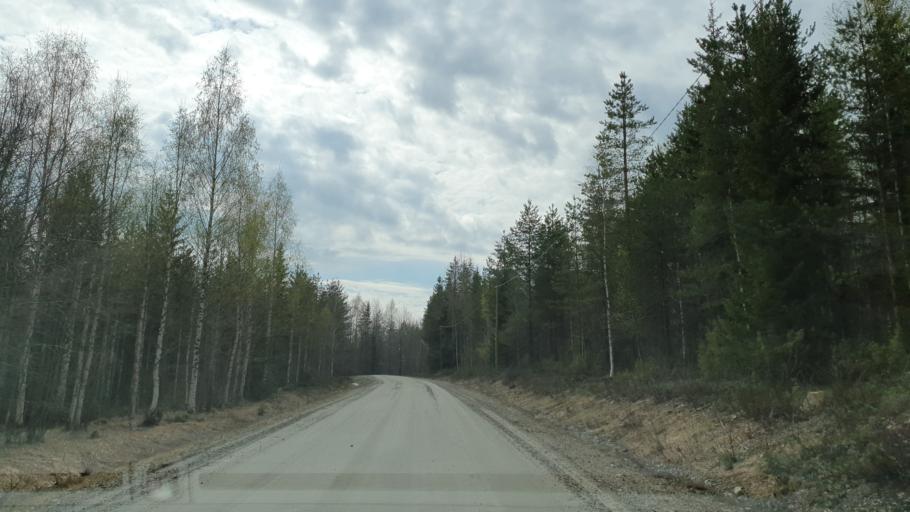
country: FI
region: Kainuu
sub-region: Kehys-Kainuu
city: Kuhmo
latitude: 64.1010
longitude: 29.9407
